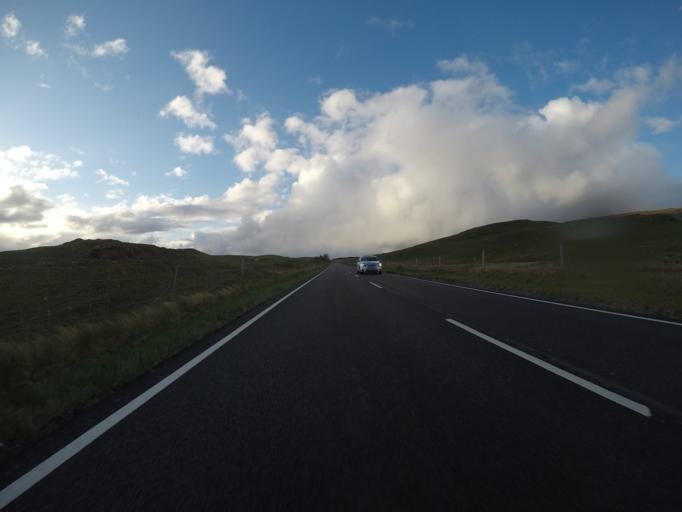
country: GB
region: Scotland
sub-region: Highland
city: Portree
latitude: 57.5431
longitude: -6.3650
